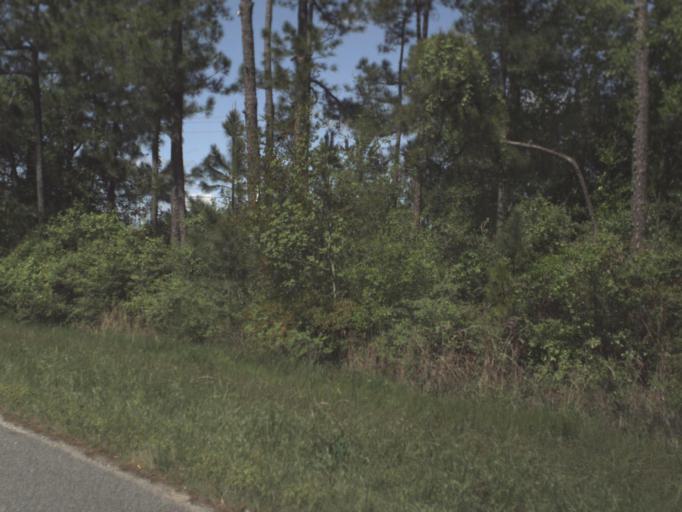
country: US
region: Florida
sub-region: Escambia County
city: Ensley
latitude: 30.5497
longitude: -87.2828
